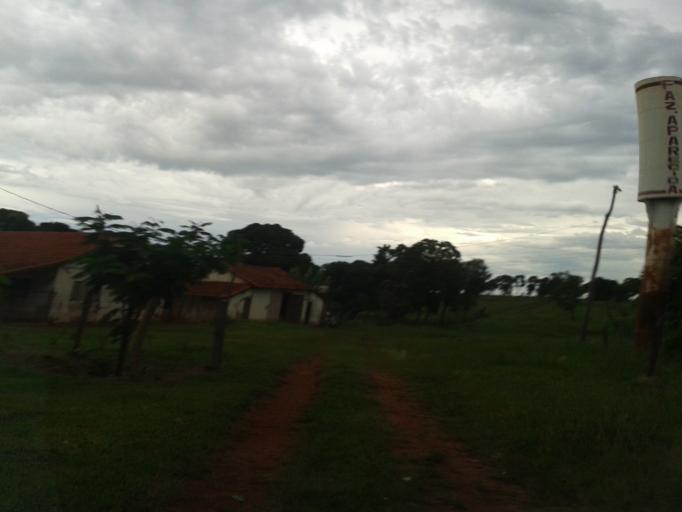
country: BR
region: Minas Gerais
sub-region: Santa Vitoria
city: Santa Vitoria
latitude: -19.2039
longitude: -50.5154
